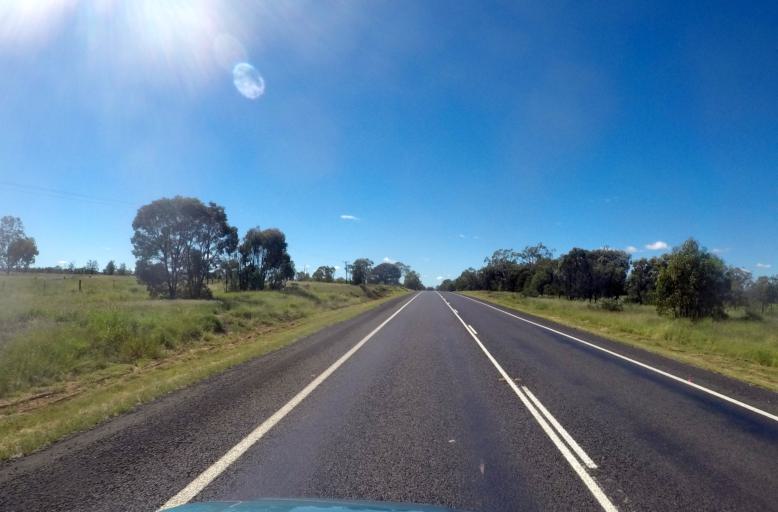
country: AU
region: Queensland
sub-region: Maranoa
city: Roma
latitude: -26.5905
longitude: 149.2255
